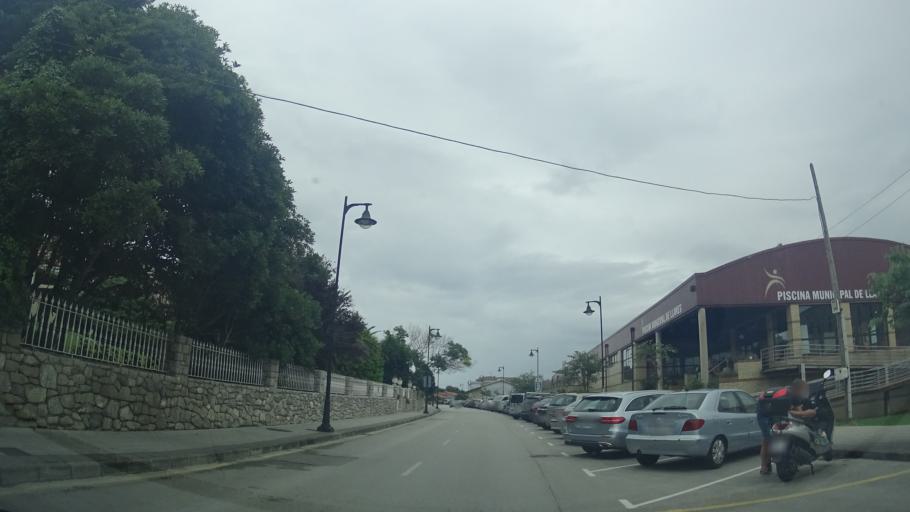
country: ES
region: Asturias
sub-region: Province of Asturias
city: Llanes
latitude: 43.4246
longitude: -4.7623
